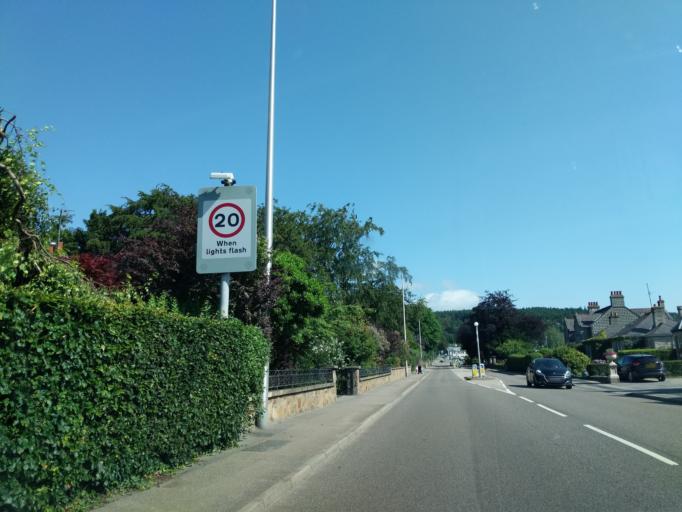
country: GB
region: Scotland
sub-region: Moray
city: Fochabers
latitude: 57.6128
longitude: -3.0928
